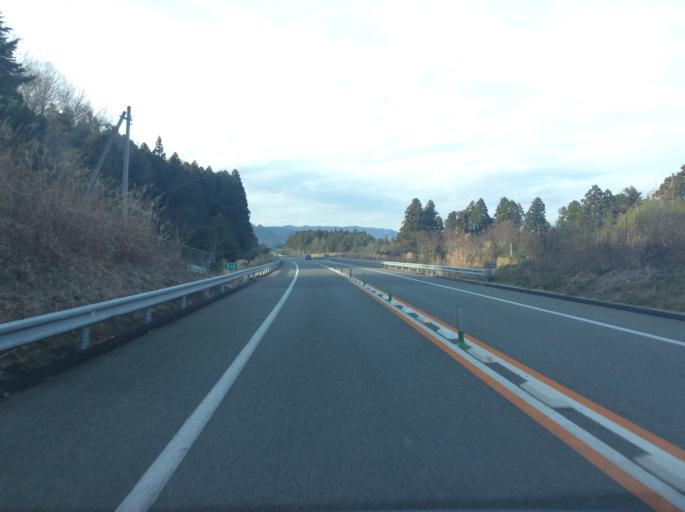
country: JP
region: Fukushima
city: Namie
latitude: 37.3481
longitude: 140.9855
